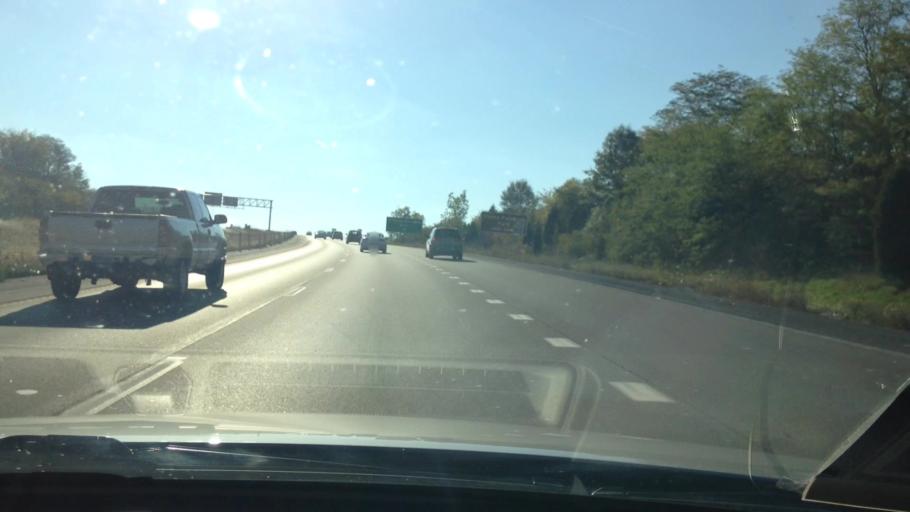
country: US
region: Missouri
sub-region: Clay County
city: Gladstone
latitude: 39.2596
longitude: -94.5937
